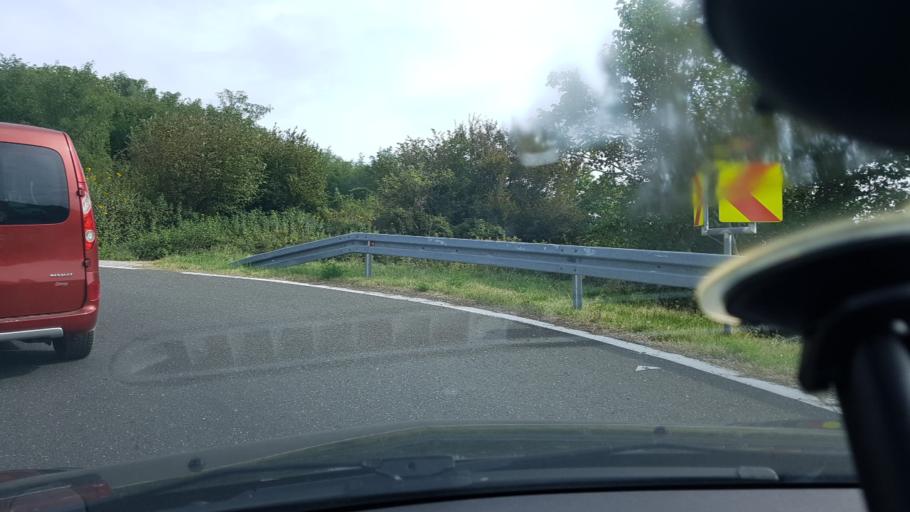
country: HR
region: Varazdinska
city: Ljubescica
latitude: 46.1101
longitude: 16.3564
